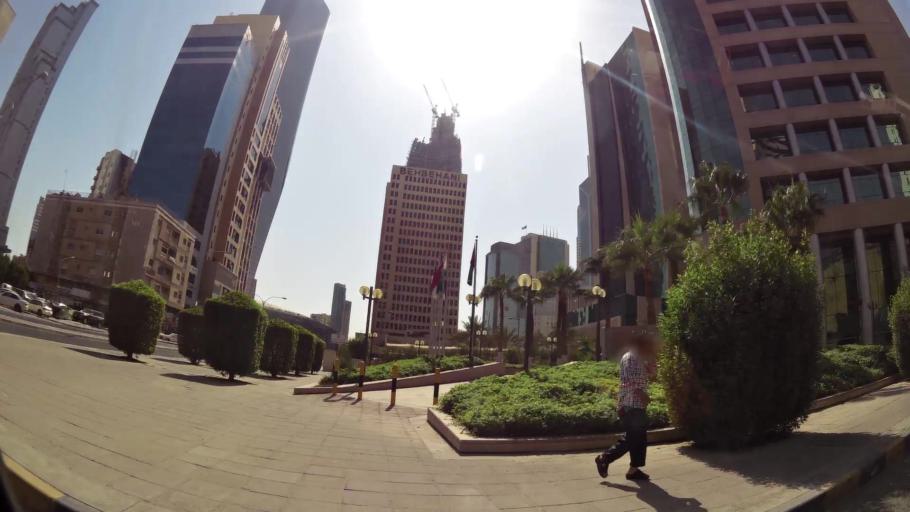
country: KW
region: Al Asimah
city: Kuwait City
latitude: 29.3816
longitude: 47.9902
